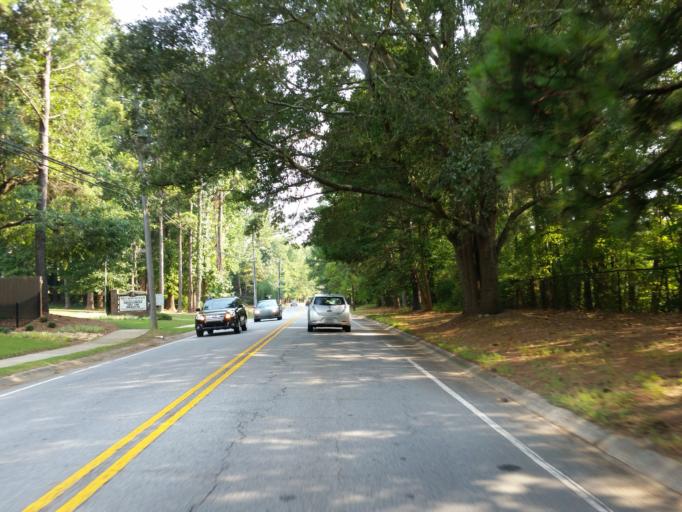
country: US
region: Georgia
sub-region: DeKalb County
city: North Atlanta
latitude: 33.8863
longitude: -84.3541
